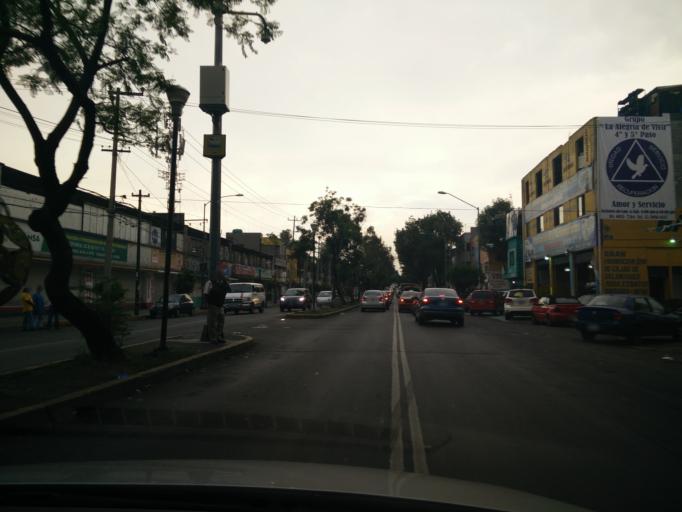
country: MX
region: Mexico City
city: Benito Juarez
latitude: 19.4061
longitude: -99.1499
